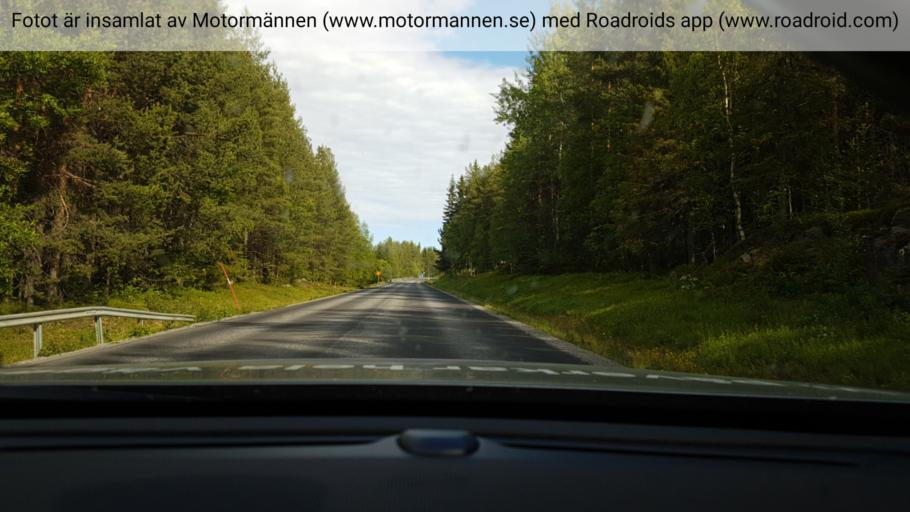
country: SE
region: Vaesterbotten
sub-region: Lycksele Kommun
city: Soderfors
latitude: 64.8286
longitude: 18.0408
